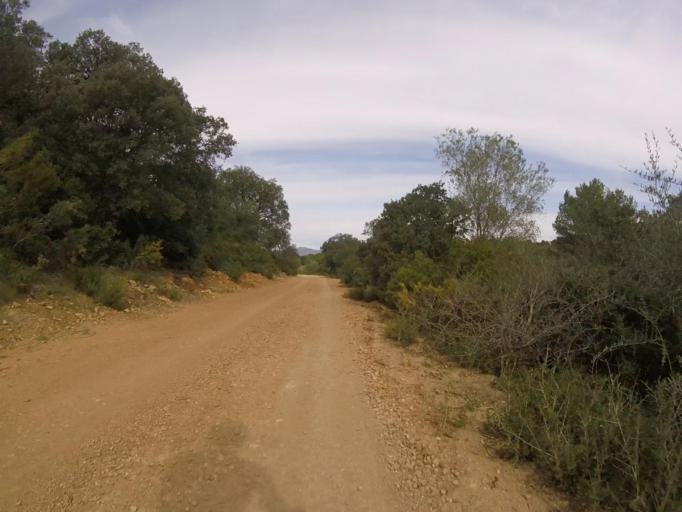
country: ES
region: Valencia
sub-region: Provincia de Castello
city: Cabanes
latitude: 40.1942
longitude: 0.0825
